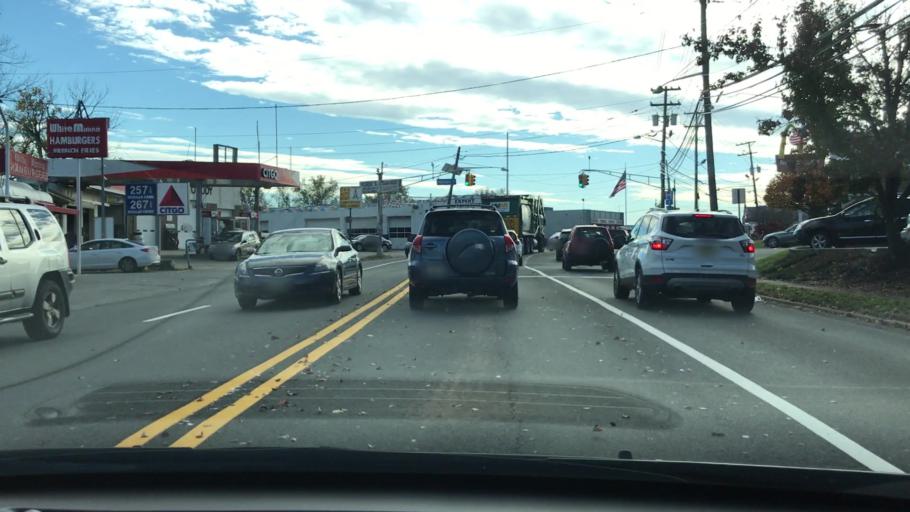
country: US
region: New Jersey
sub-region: Bergen County
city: Hackensack
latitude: 40.8894
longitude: -74.0387
